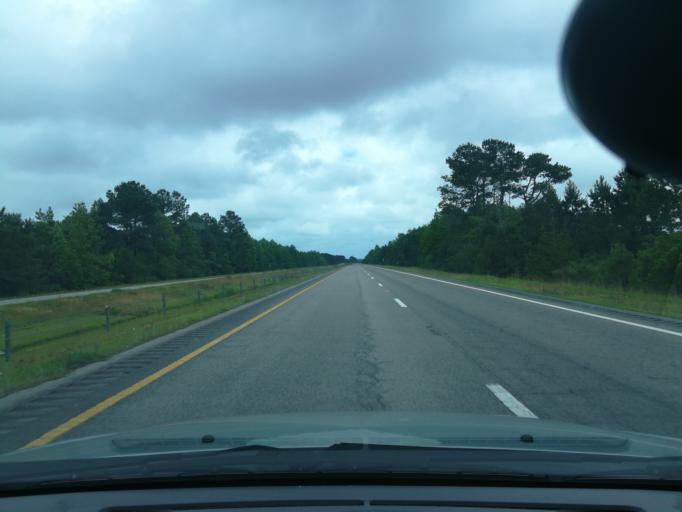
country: US
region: North Carolina
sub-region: Chowan County
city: Edenton
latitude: 35.8991
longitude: -76.5046
